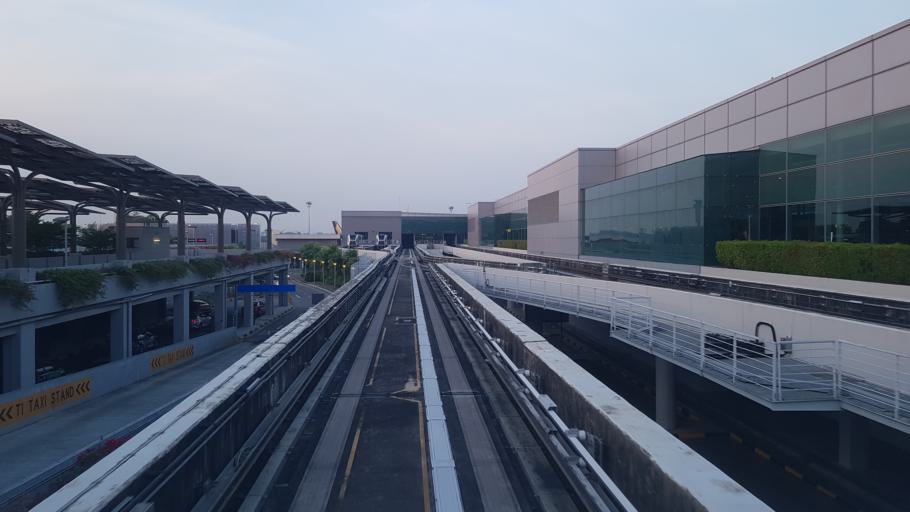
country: SG
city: Singapore
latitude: 1.3520
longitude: 103.9847
